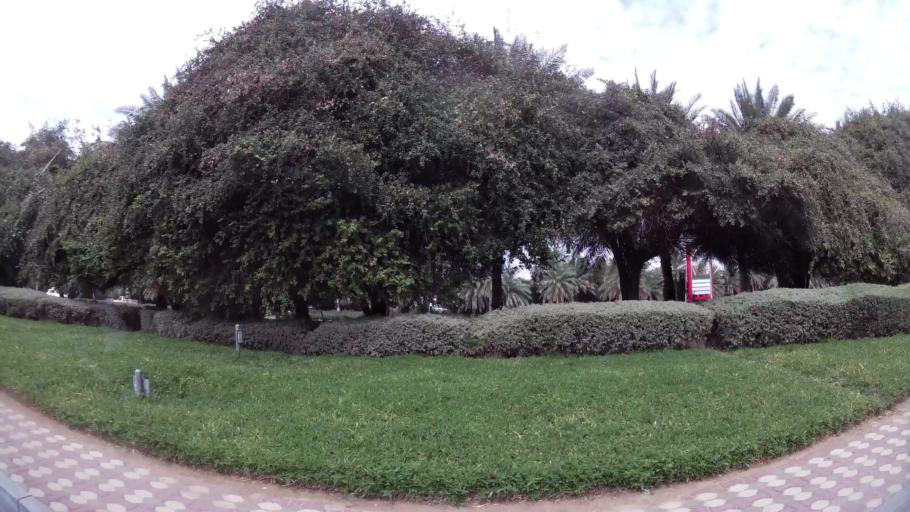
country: AE
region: Abu Dhabi
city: Al Ain
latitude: 24.2052
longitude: 55.7946
